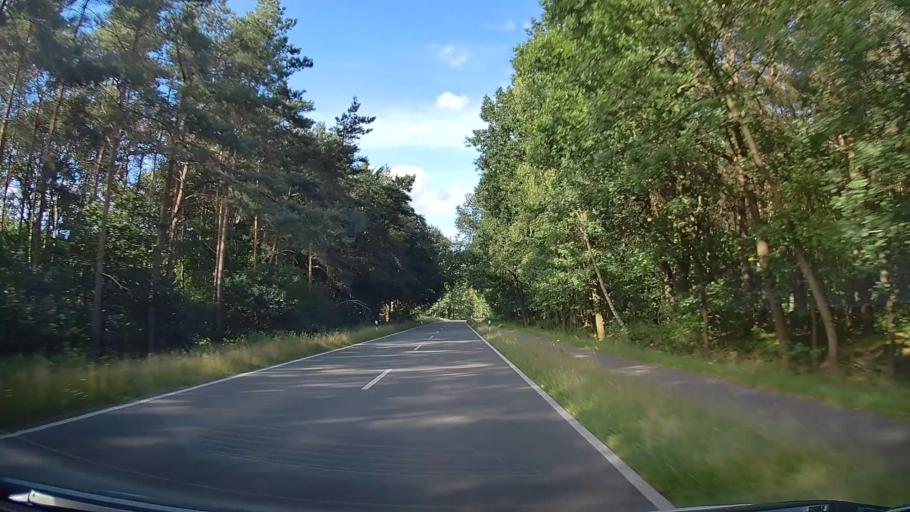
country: DE
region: Lower Saxony
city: Bosel
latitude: 52.9594
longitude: 7.9067
